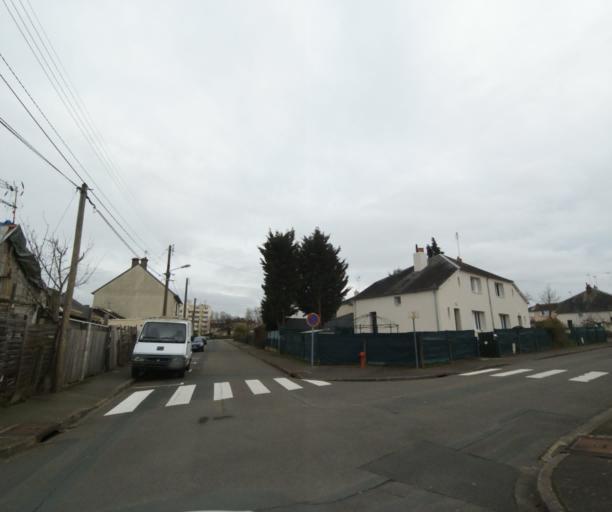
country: FR
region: Pays de la Loire
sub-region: Departement de la Sarthe
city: Le Mans
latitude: 47.9735
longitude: 0.2033
